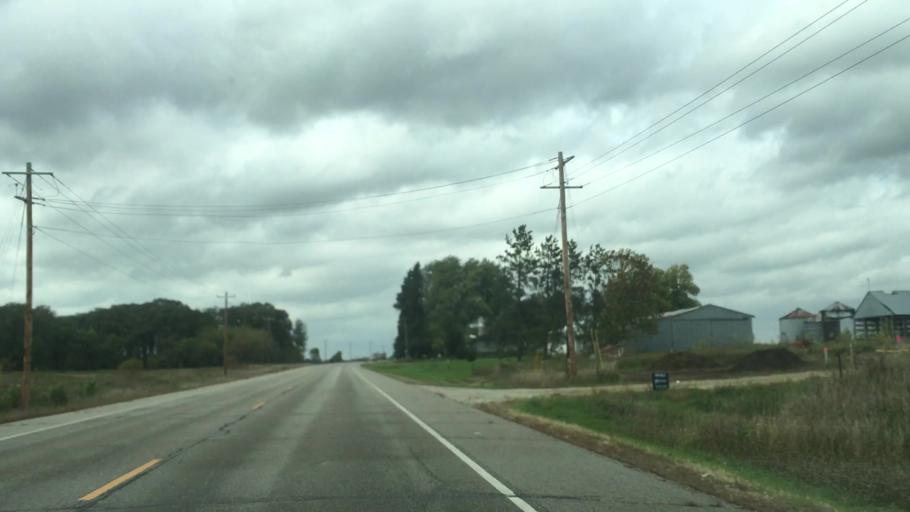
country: US
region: Minnesota
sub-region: Olmsted County
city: Eyota
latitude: 43.9089
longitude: -92.2663
